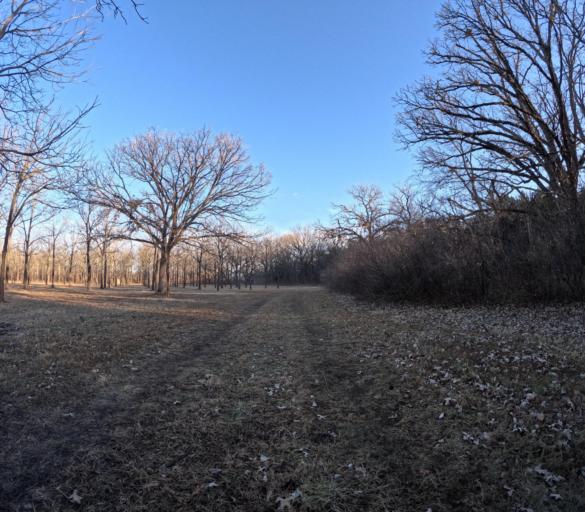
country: US
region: Kansas
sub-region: Riley County
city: Ogden
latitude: 39.2028
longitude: -96.6841
